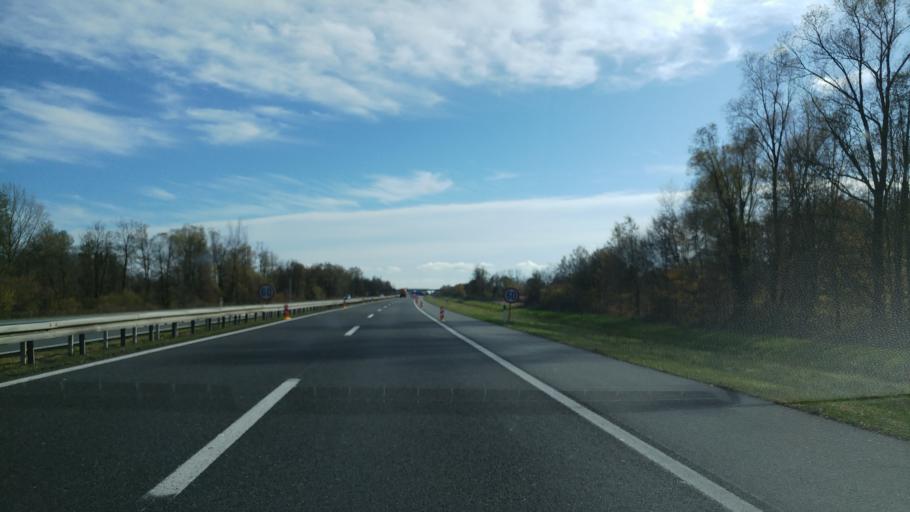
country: HR
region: Sisacko-Moslavacka
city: Husain
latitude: 45.4378
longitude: 16.8265
